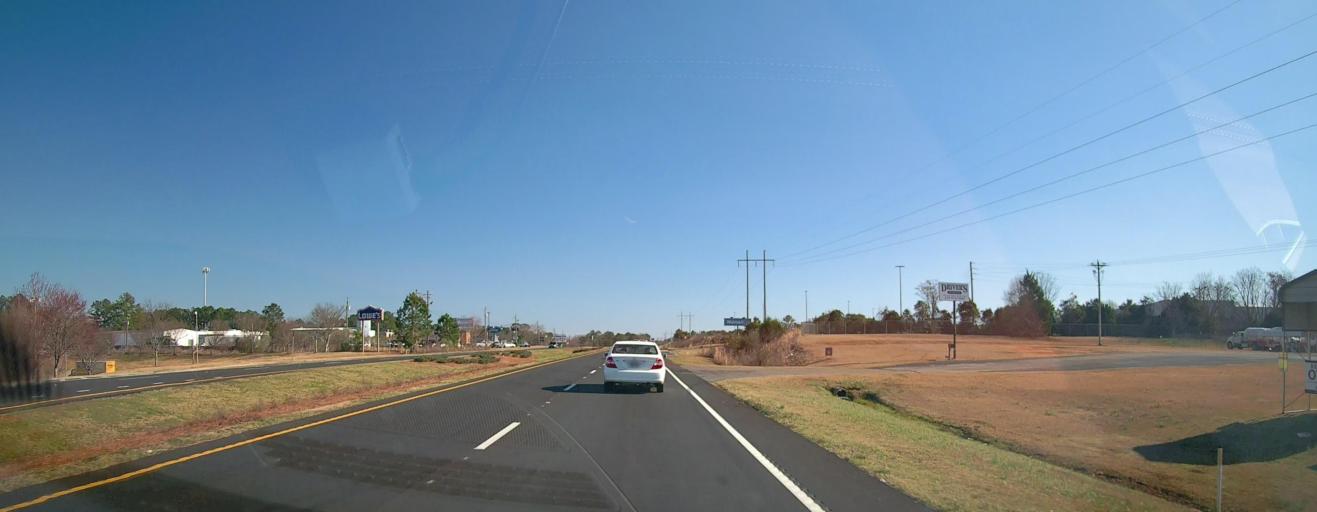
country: US
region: Georgia
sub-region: Sumter County
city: Americus
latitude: 32.0630
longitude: -84.2016
